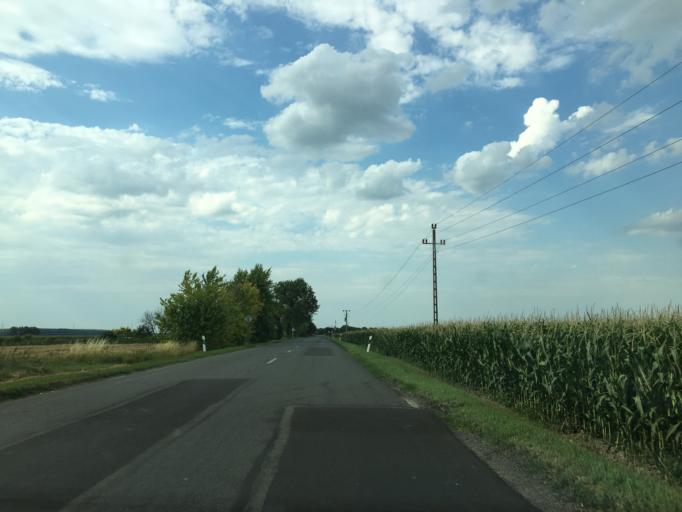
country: HU
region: Bacs-Kiskun
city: Dusnok
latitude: 46.4264
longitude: 18.9450
